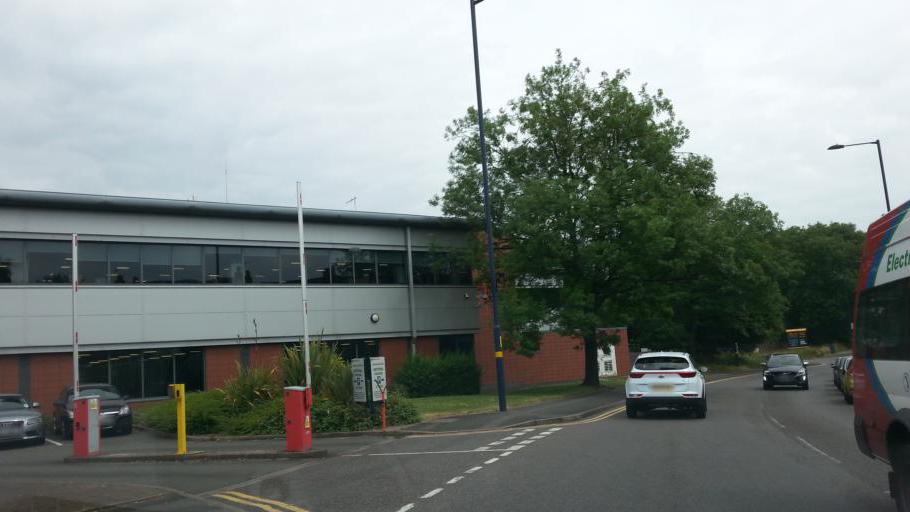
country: GB
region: England
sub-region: City and Borough of Birmingham
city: Birmingham
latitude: 52.4229
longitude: -1.9197
